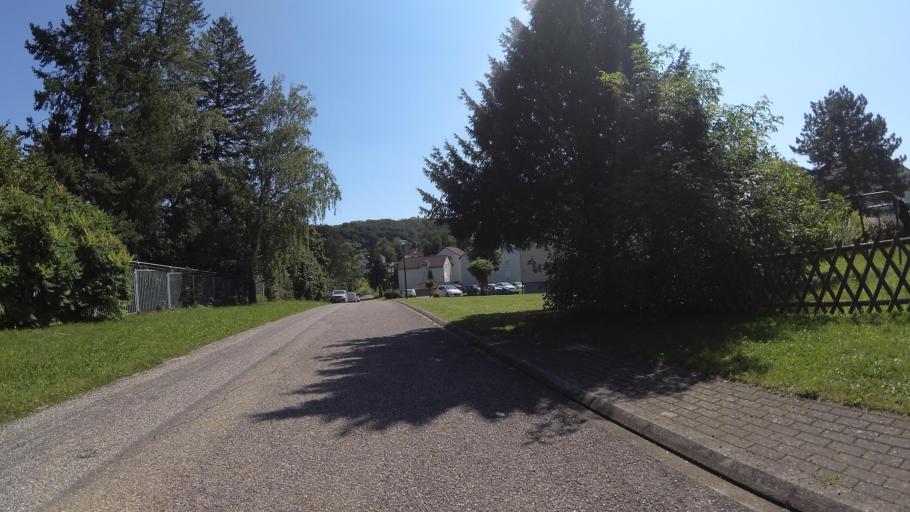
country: FR
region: Lorraine
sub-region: Departement de la Moselle
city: Spicheren
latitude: 49.2059
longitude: 6.9540
